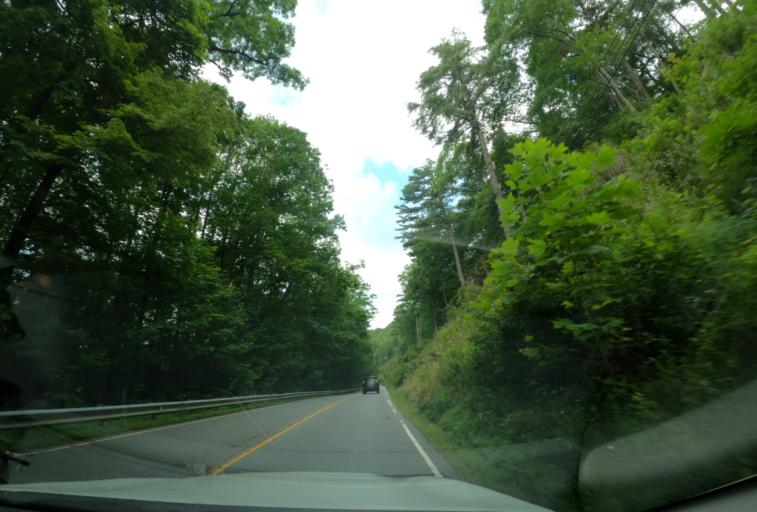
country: US
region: North Carolina
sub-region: Jackson County
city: Cullowhee
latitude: 35.1078
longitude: -83.1253
